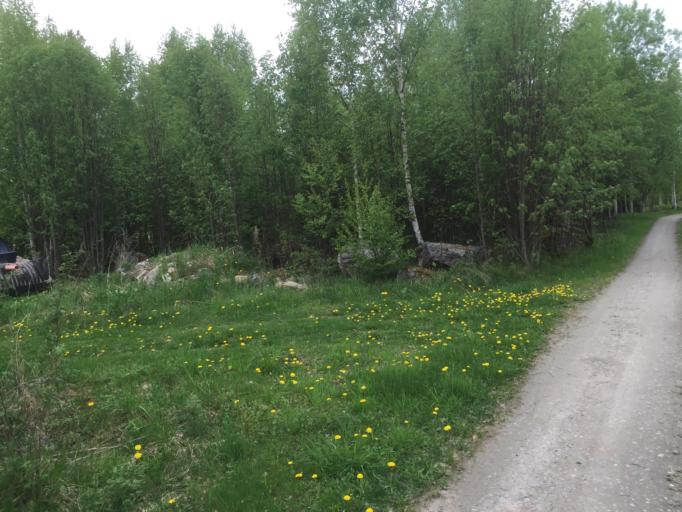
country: SE
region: Uppsala
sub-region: Alvkarleby Kommun
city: Skutskaer
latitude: 60.7908
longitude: 17.2968
